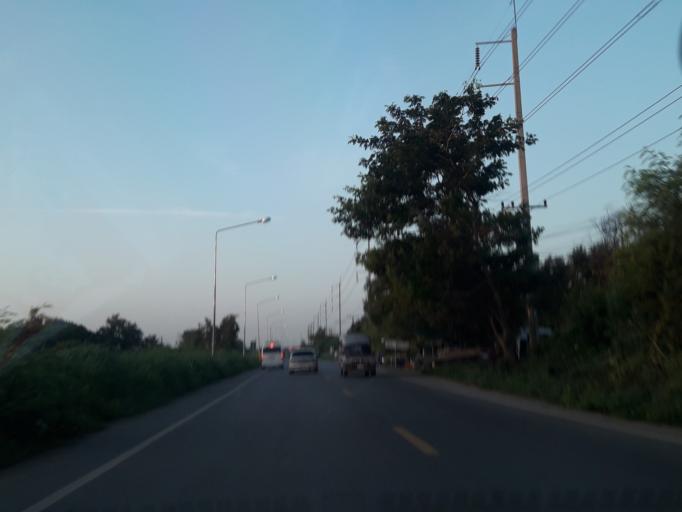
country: TH
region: Phra Nakhon Si Ayutthaya
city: Bang Pahan
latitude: 14.4745
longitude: 100.5520
